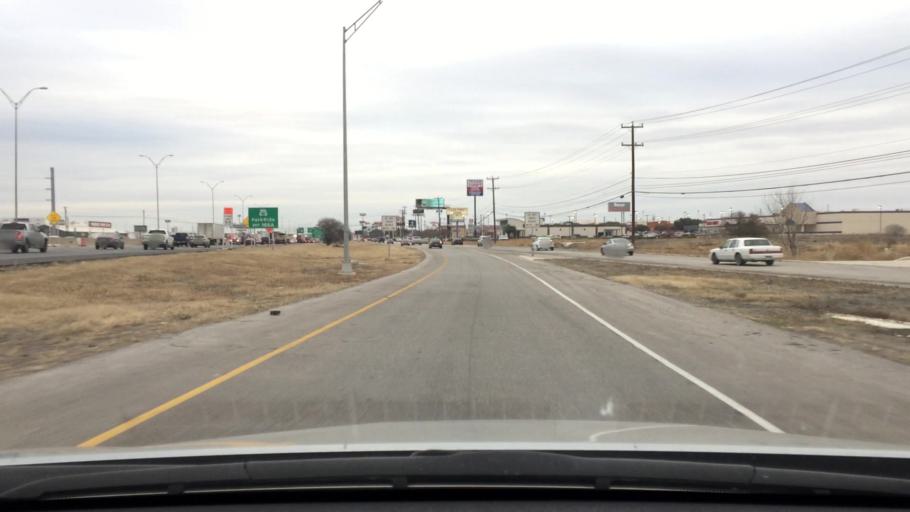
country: US
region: Texas
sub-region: Bexar County
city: Windcrest
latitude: 29.4994
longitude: -98.3996
